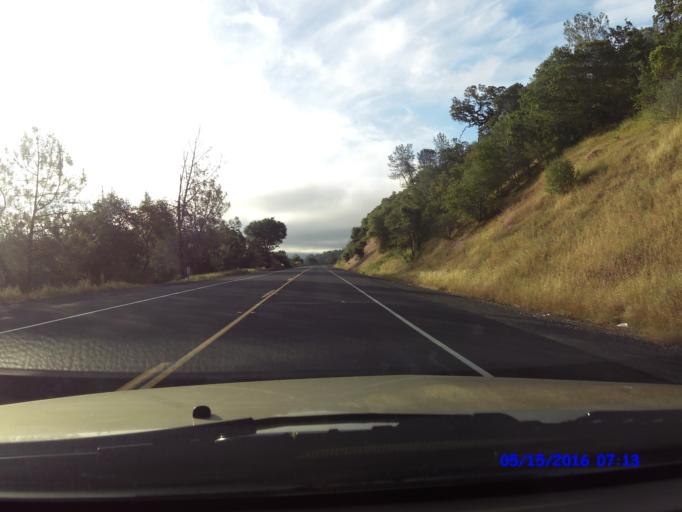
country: US
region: California
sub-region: Tuolumne County
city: Jamestown
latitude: 37.8387
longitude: -120.3660
